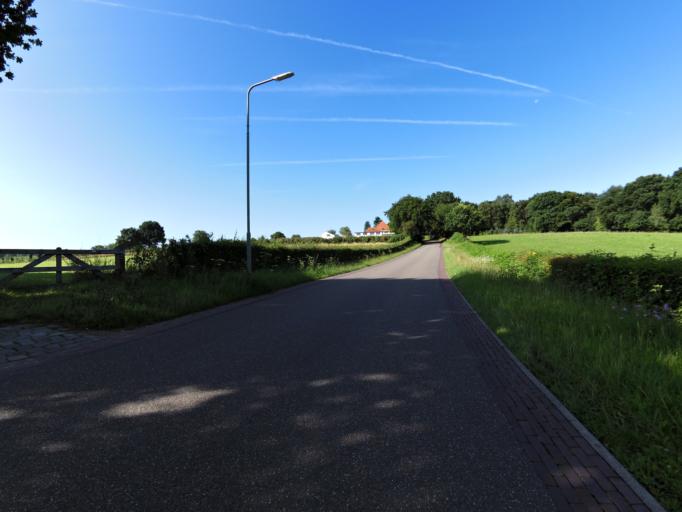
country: BE
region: Wallonia
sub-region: Province de Liege
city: Plombieres
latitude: 50.7795
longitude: 5.8946
